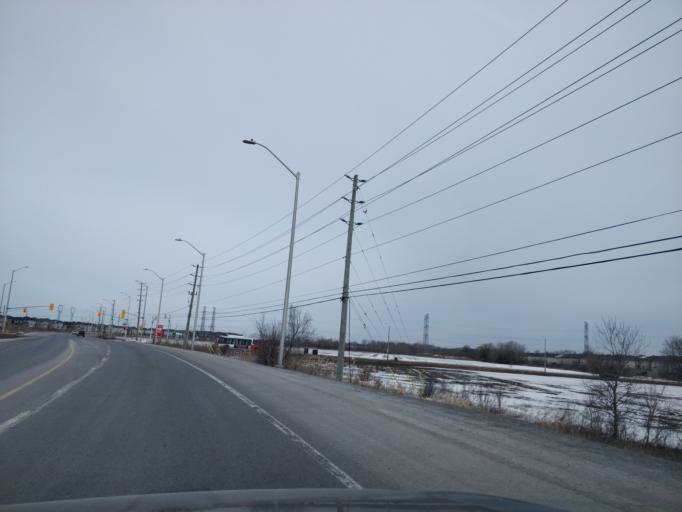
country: CA
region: Ontario
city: Bells Corners
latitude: 45.2759
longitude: -75.8711
